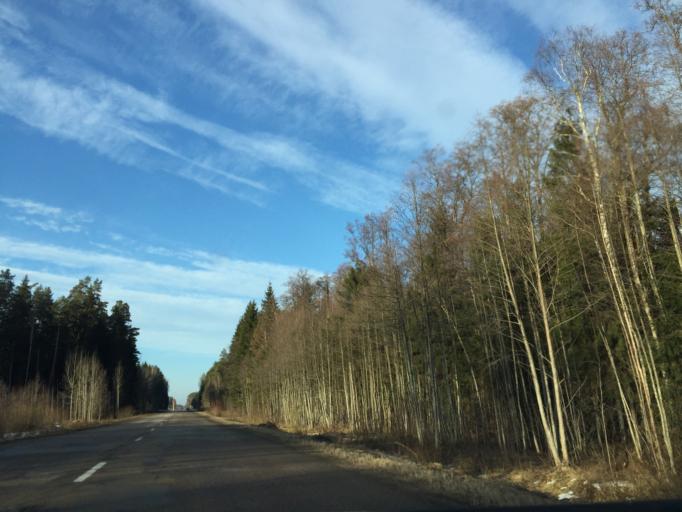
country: LV
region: Lecava
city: Iecava
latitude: 56.7086
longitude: 24.1130
